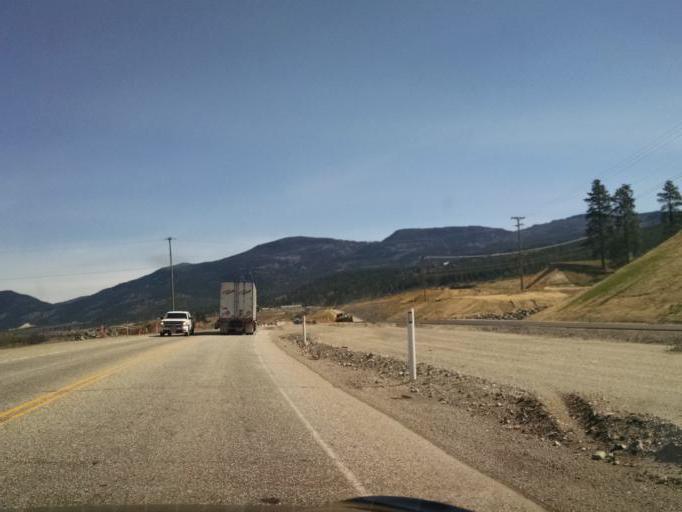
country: CA
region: British Columbia
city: Chase
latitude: 50.6701
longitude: -119.8516
